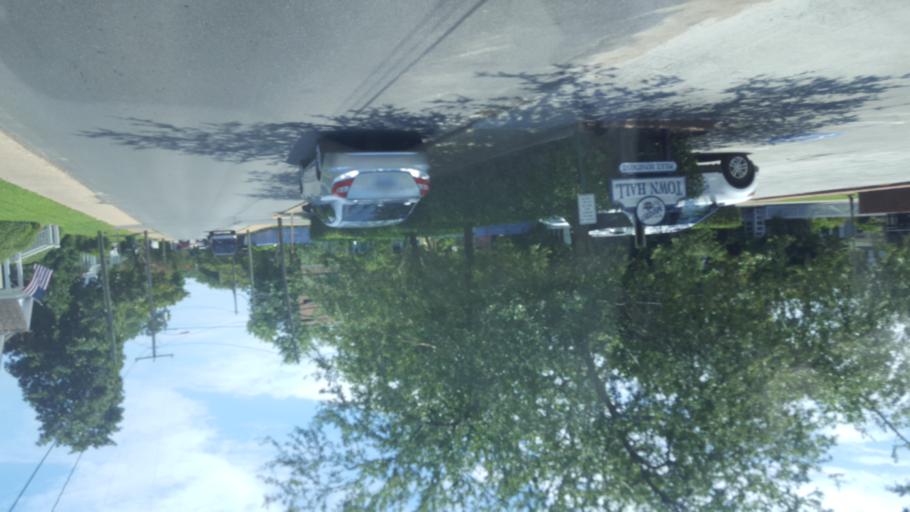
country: US
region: North Carolina
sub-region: Dare County
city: Manteo
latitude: 35.9093
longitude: -75.6743
